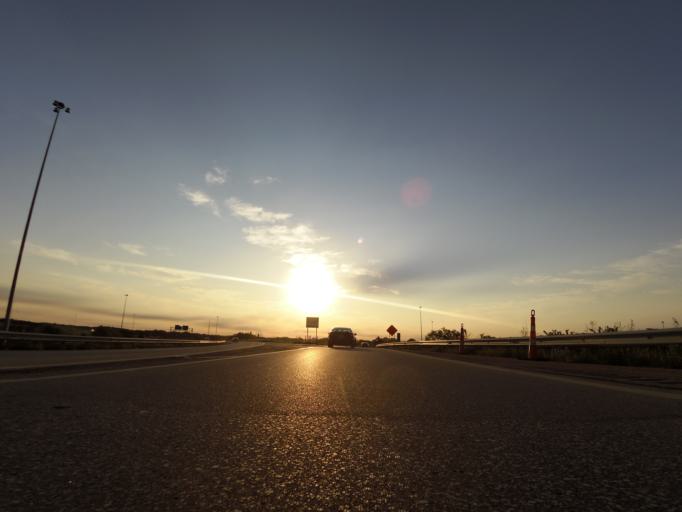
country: US
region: Kansas
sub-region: Sedgwick County
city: Park City
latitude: 37.7588
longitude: -97.3250
